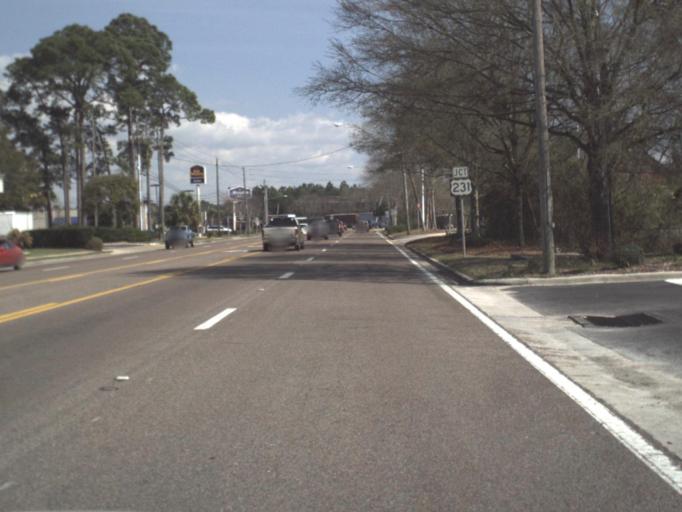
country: US
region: Florida
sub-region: Bay County
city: Hiland Park
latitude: 30.1895
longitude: -85.6433
